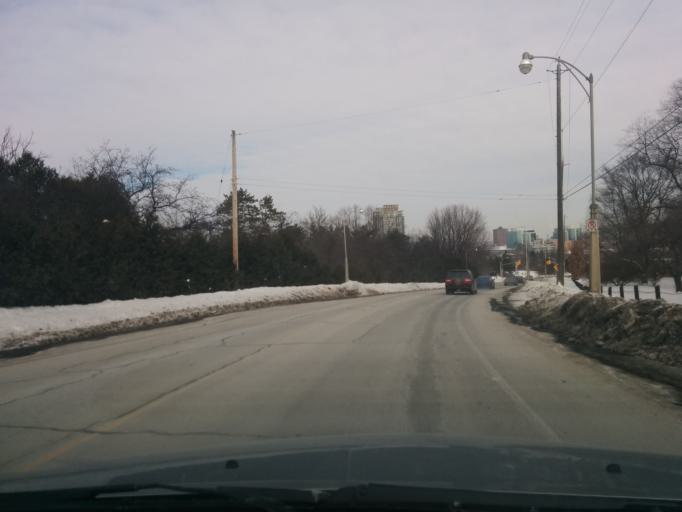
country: CA
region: Ontario
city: Ottawa
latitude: 45.3923
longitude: -75.7082
